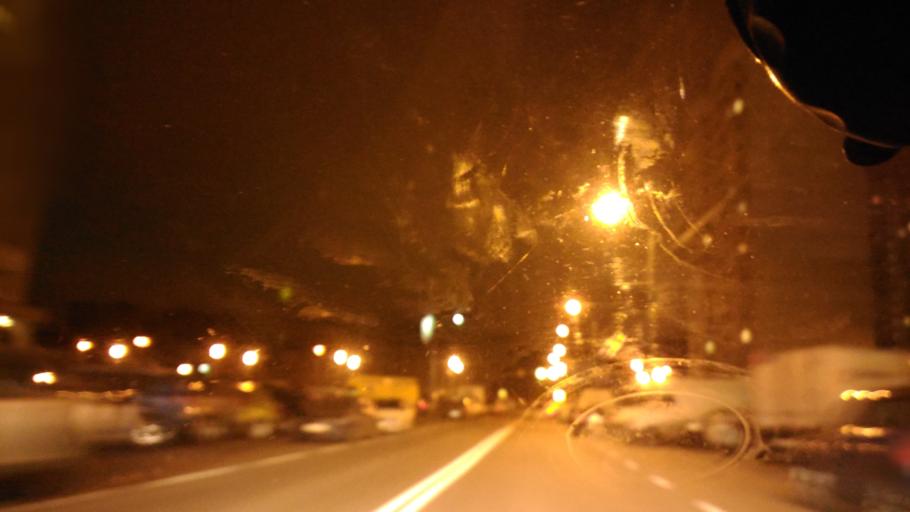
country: RU
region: Moskovskaya
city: Pavshino
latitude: 55.8235
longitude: 37.3665
